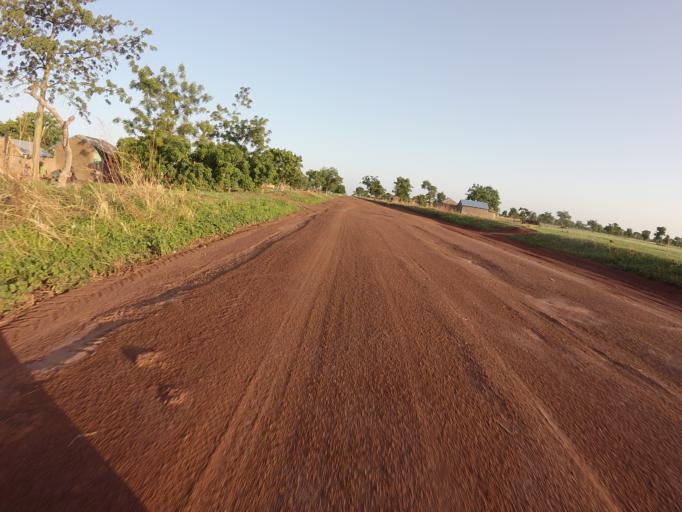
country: TG
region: Savanes
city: Sansanne-Mango
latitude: 10.2670
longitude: -0.0809
